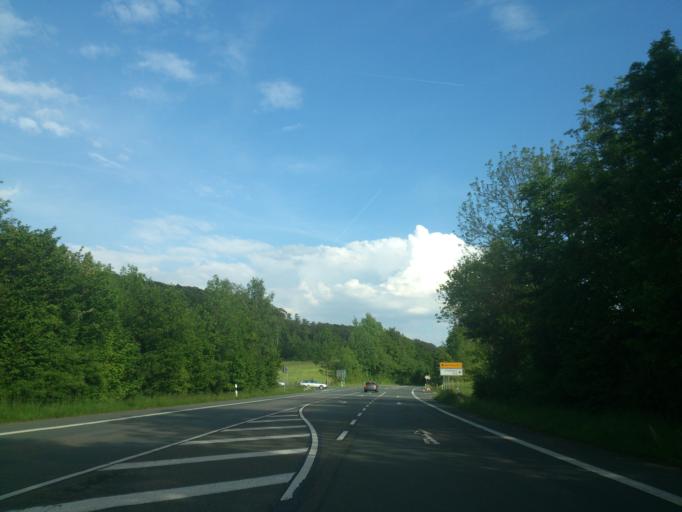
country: DE
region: North Rhine-Westphalia
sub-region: Regierungsbezirk Detmold
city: Willebadessen
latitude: 51.6688
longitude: 9.0005
